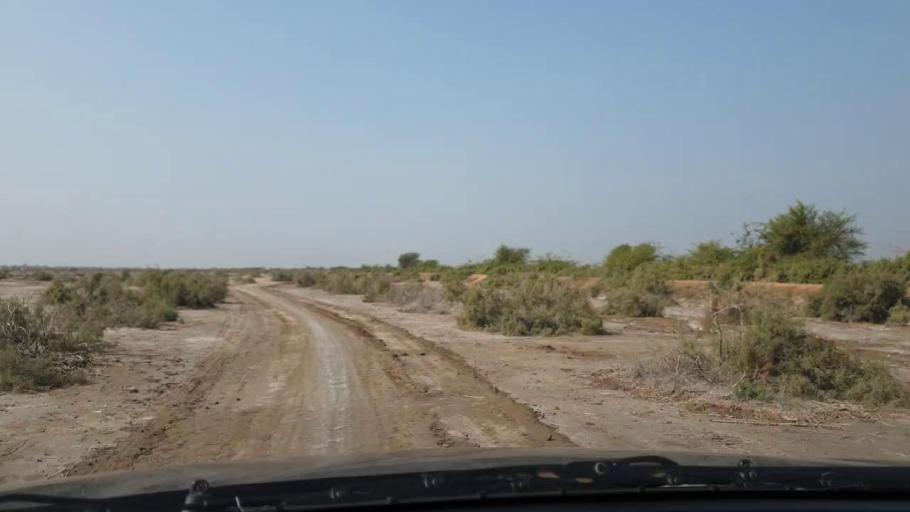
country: PK
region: Sindh
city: Jhol
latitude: 25.8893
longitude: 68.9749
